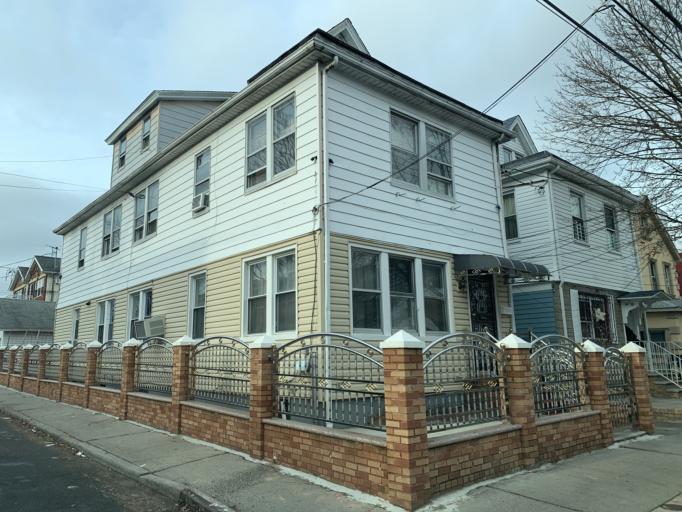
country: US
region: New York
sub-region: Queens County
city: Jamaica
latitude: 40.6902
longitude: -73.8035
